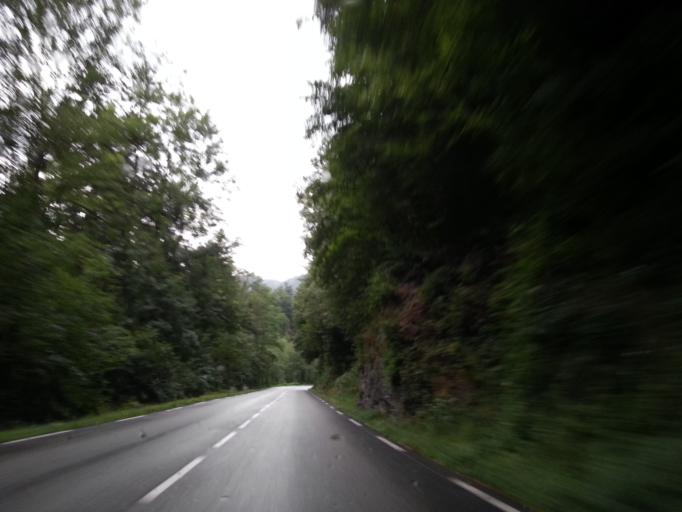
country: FR
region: Rhone-Alpes
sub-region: Departement de la Savoie
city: Marthod
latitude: 45.7154
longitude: 6.4696
